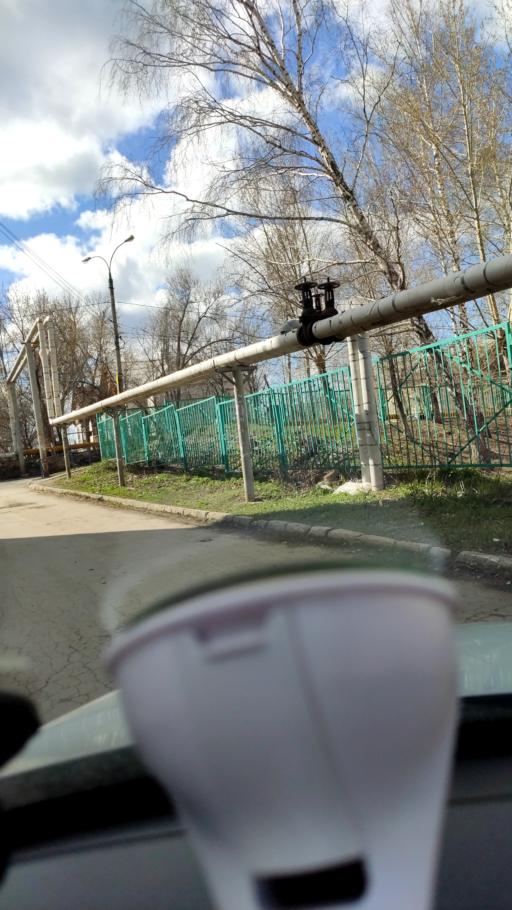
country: RU
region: Samara
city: Volzhskiy
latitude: 53.3448
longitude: 50.2130
